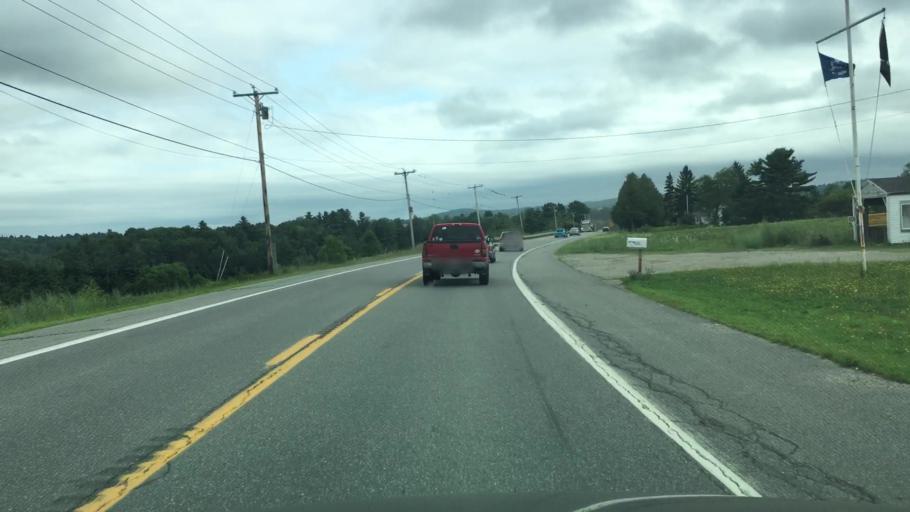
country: US
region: Maine
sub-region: Waldo County
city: Frankfort
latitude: 44.5635
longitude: -68.8666
